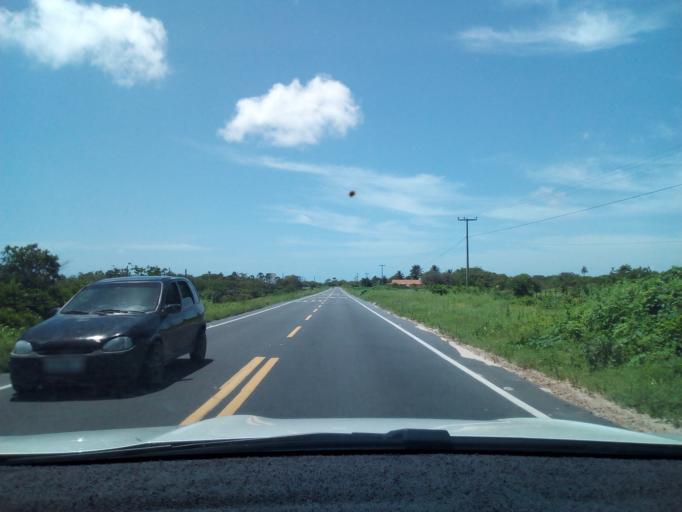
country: BR
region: Ceara
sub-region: Aracati
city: Aracati
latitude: -4.3954
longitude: -37.8586
